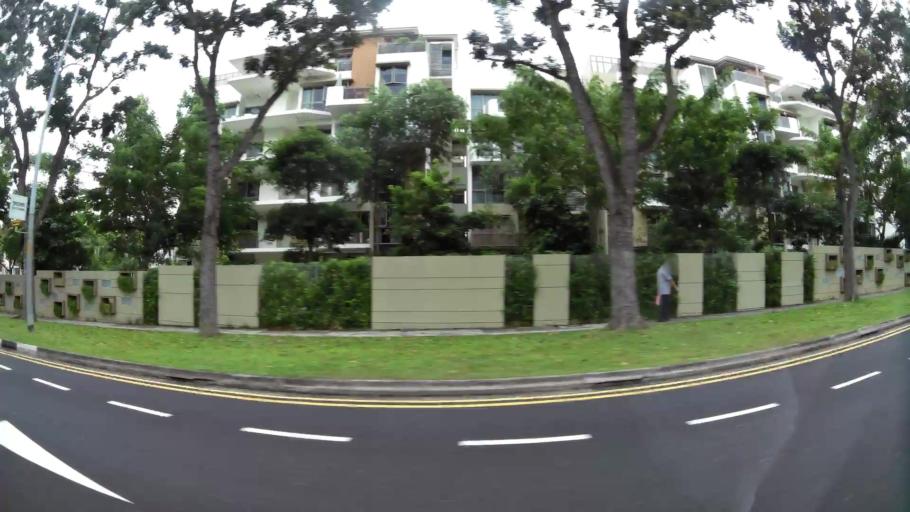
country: SG
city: Singapore
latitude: 1.3694
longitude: 103.8790
